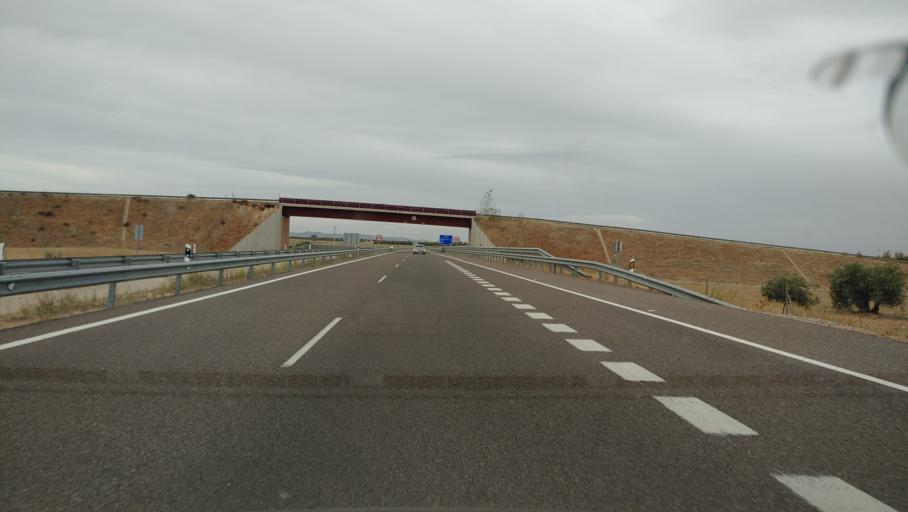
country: ES
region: Castille-La Mancha
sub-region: Provincia de Ciudad Real
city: Valenzuela de Calatrava
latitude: 38.8997
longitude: -3.8209
